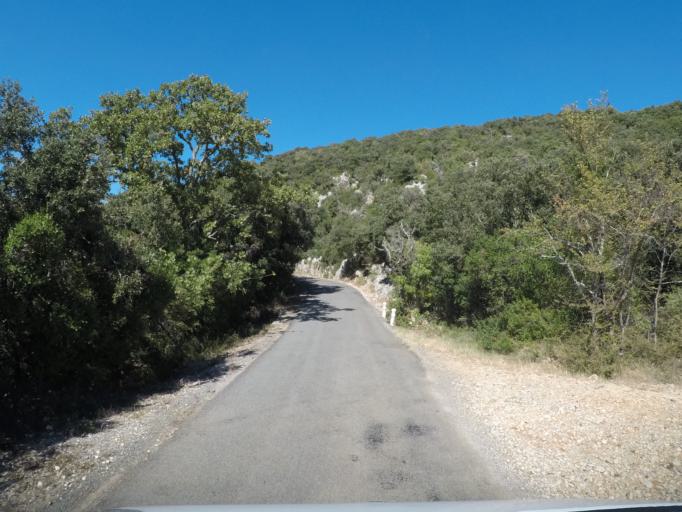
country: FR
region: Languedoc-Roussillon
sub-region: Departement de l'Herault
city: Vailhauques
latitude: 43.7190
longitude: 3.6813
